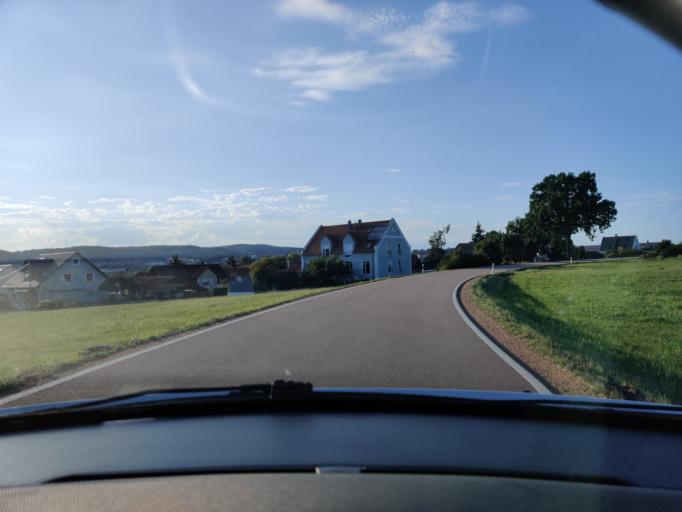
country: DE
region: Bavaria
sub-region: Upper Palatinate
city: Nabburg
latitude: 49.4399
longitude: 12.1911
